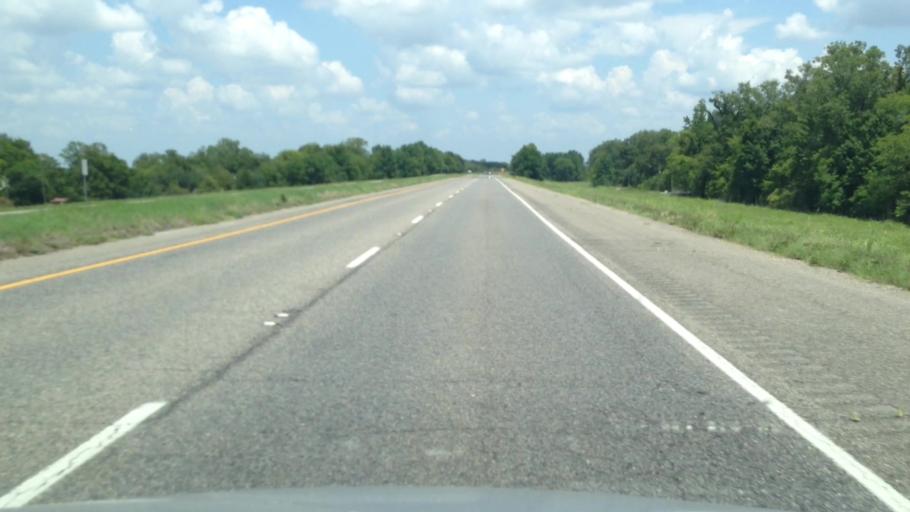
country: US
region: Louisiana
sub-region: Saint Landry Parish
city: Krotz Springs
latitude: 30.5487
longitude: -91.8414
